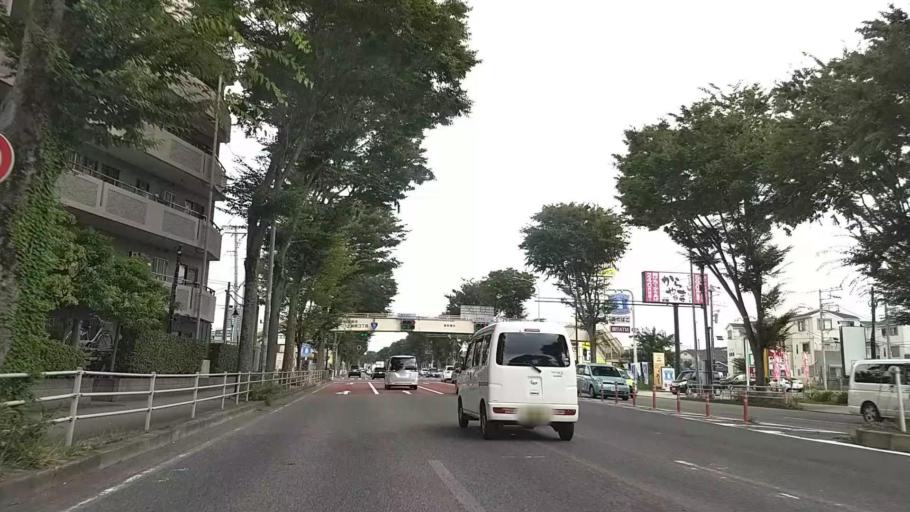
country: JP
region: Tokyo
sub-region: Machida-shi
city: Machida
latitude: 35.5222
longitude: 139.4508
